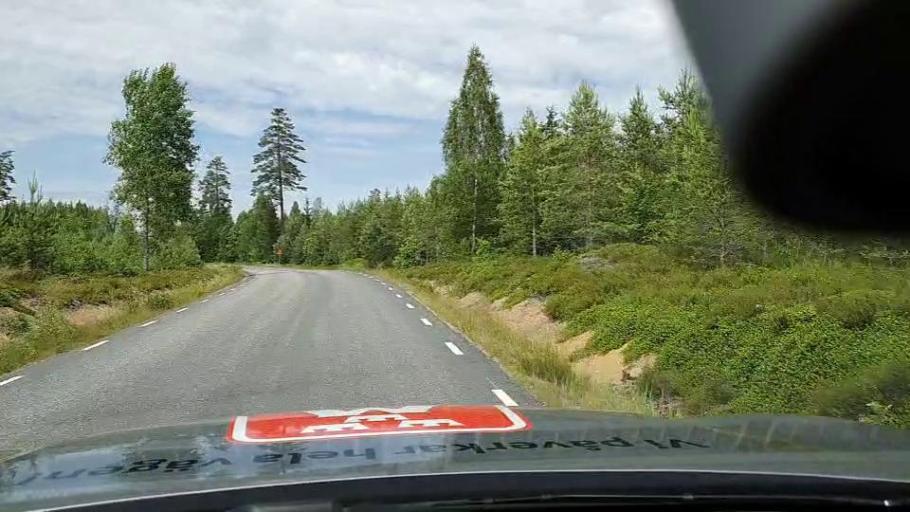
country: SE
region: Soedermanland
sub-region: Eskilstuna Kommun
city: Arla
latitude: 59.2390
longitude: 16.7220
